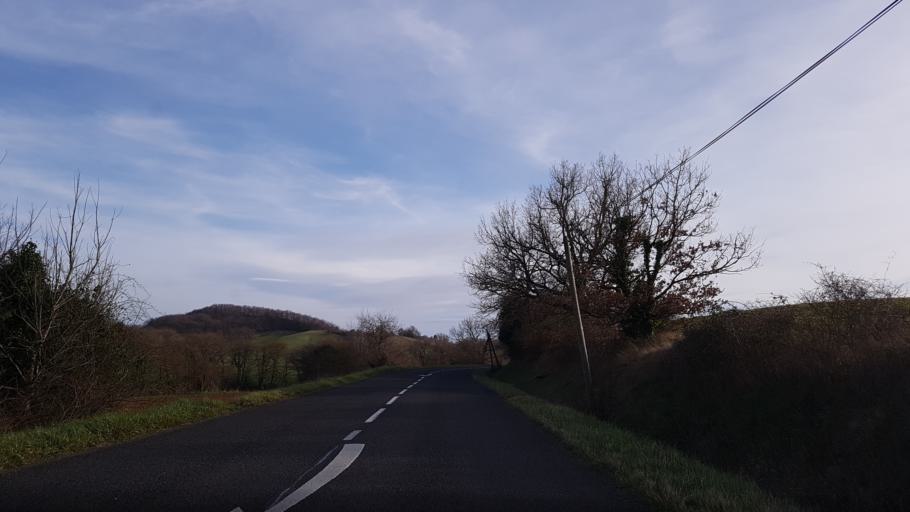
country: FR
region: Midi-Pyrenees
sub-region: Departement de l'Ariege
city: Mirepoix
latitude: 43.1437
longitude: 1.9128
